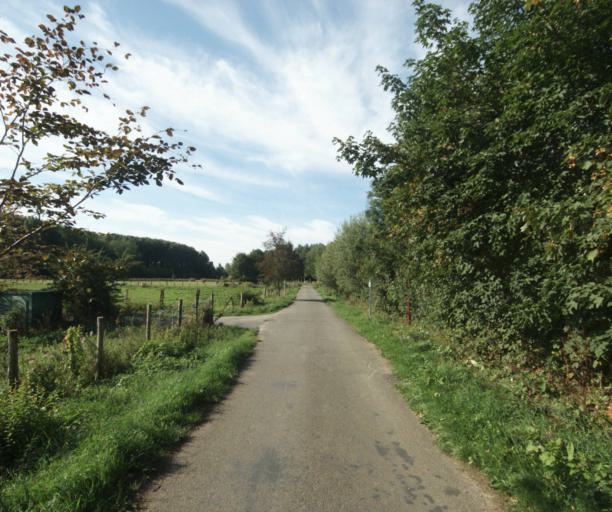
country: FR
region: Nord-Pas-de-Calais
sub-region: Departement du Nord
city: Sainghin-en-Melantois
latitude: 50.5870
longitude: 3.1813
